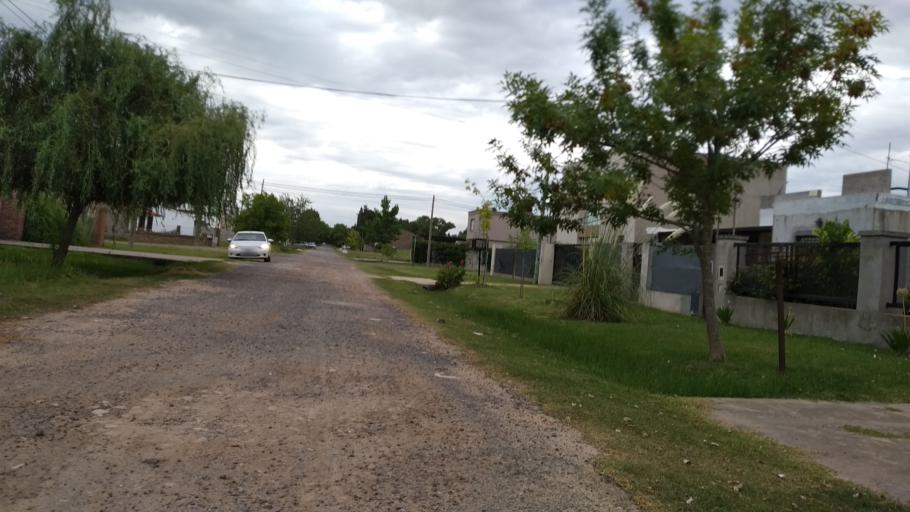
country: AR
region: Santa Fe
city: Funes
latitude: -32.9320
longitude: -60.8014
